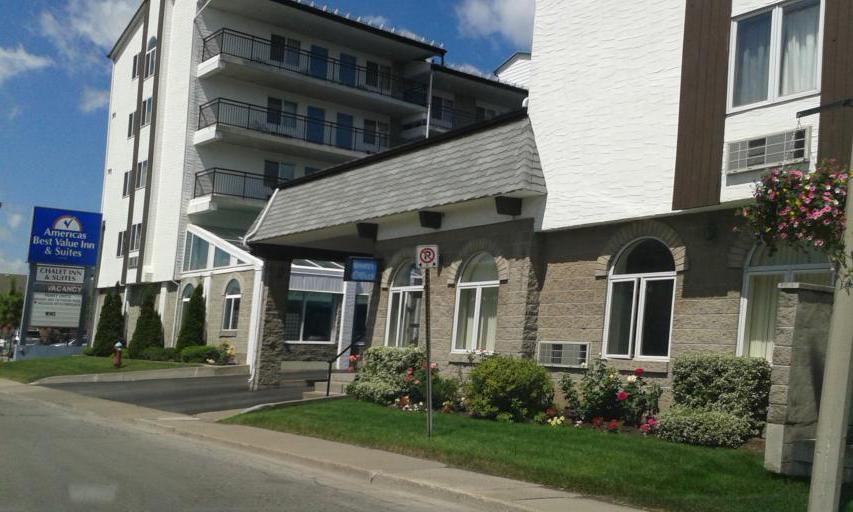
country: CA
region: Ontario
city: Niagara Falls
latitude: 43.0939
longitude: -79.0752
